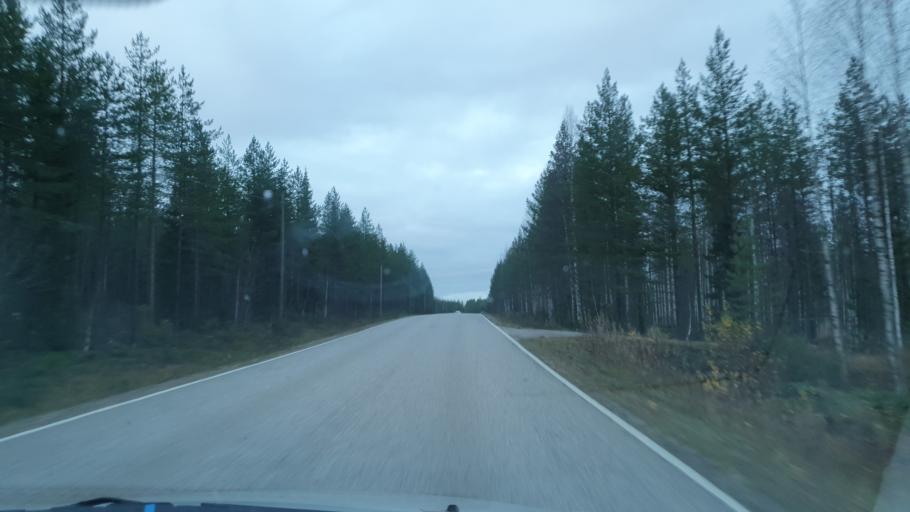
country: FI
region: Kainuu
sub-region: Kajaani
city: Ristijaervi
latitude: 64.4327
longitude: 28.3685
